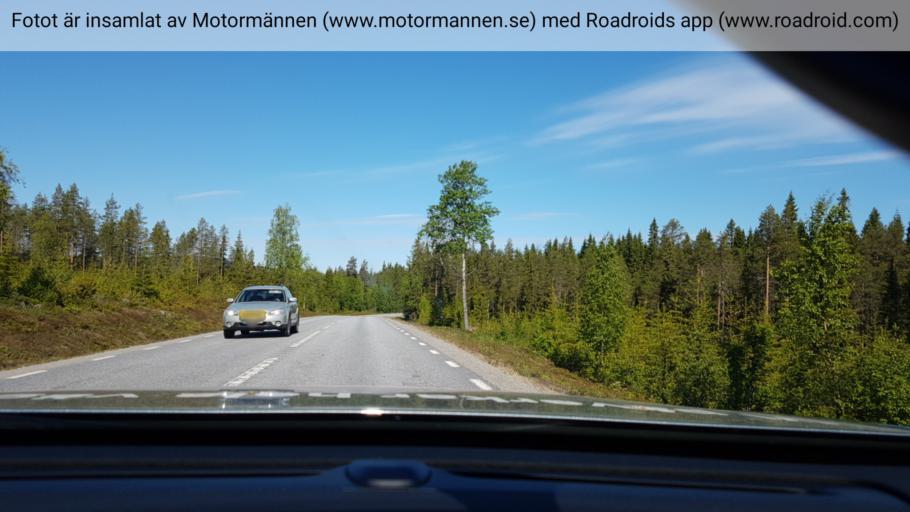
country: SE
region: Vaesterbotten
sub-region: Bjurholms Kommun
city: Bjurholm
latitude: 63.9605
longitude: 18.8582
